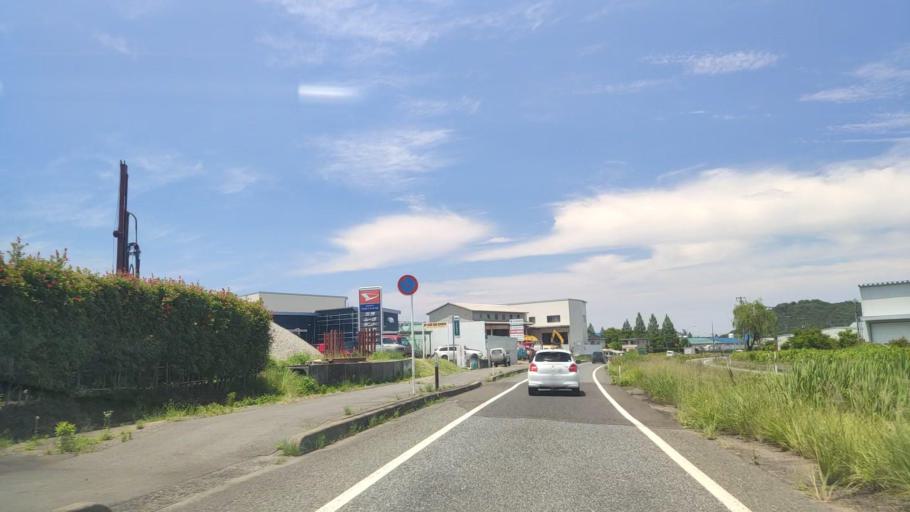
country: JP
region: Tottori
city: Tottori
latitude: 35.4536
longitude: 134.2443
